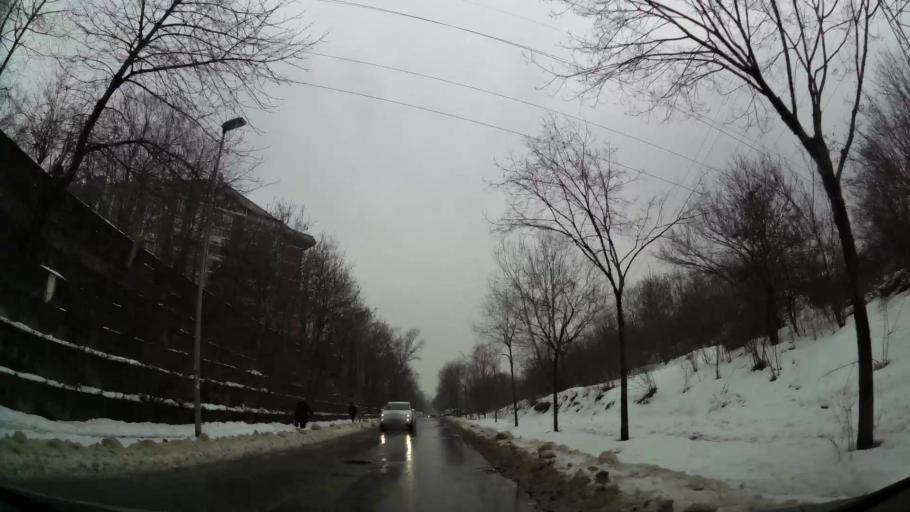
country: RS
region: Central Serbia
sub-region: Belgrade
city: Zvezdara
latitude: 44.7739
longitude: 20.5086
